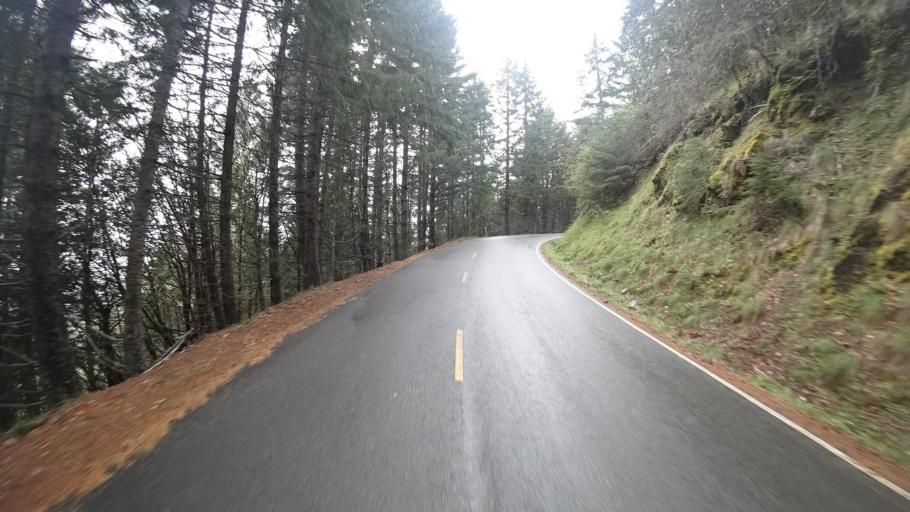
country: US
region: California
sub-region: Humboldt County
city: Westhaven-Moonstone
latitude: 41.1471
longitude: -123.8422
